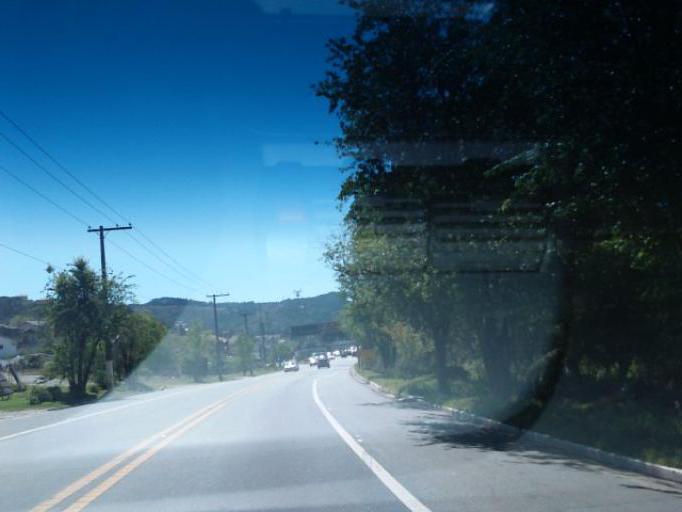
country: BR
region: Sao Paulo
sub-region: Campos Do Jordao
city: Campos do Jordao
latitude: -22.7572
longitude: -45.6106
